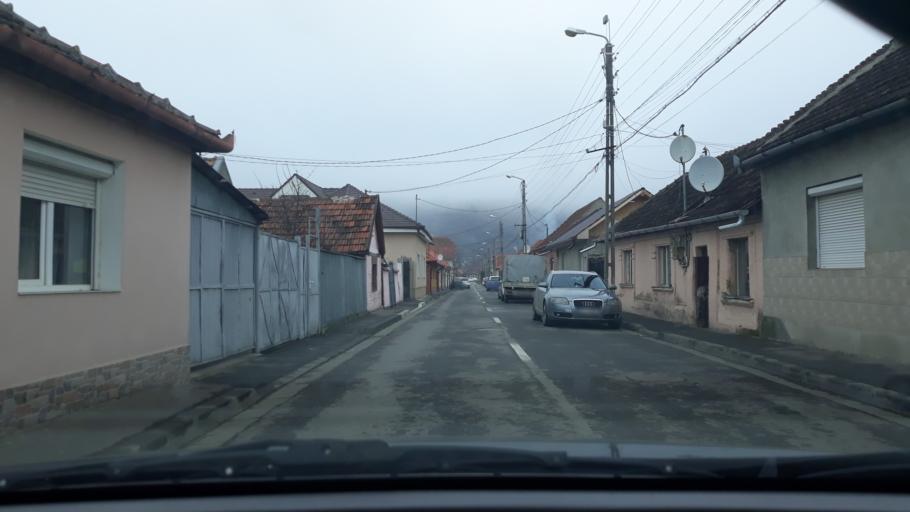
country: RO
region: Bihor
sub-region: Comuna Sanmartin
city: Sanmartin
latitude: 47.0472
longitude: 21.9725
